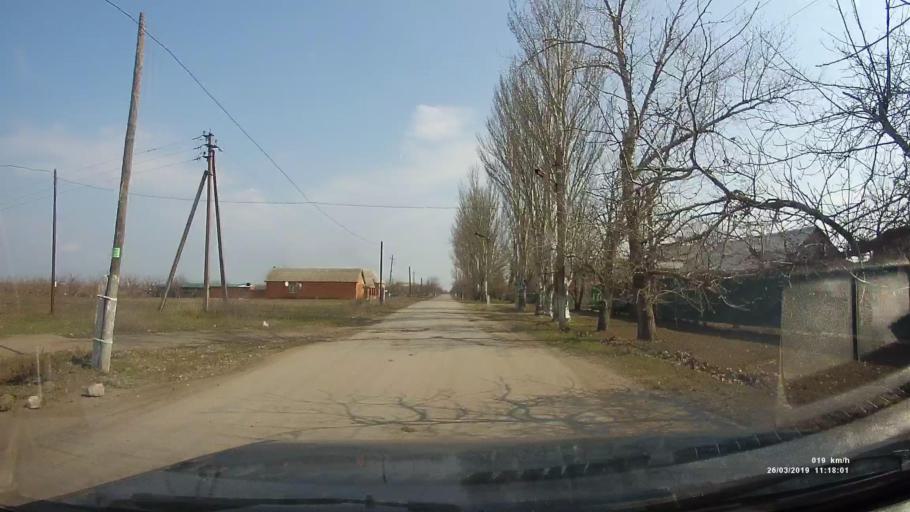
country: RU
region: Krasnodarskiy
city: Shabel'skoye
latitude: 47.1314
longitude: 38.5303
